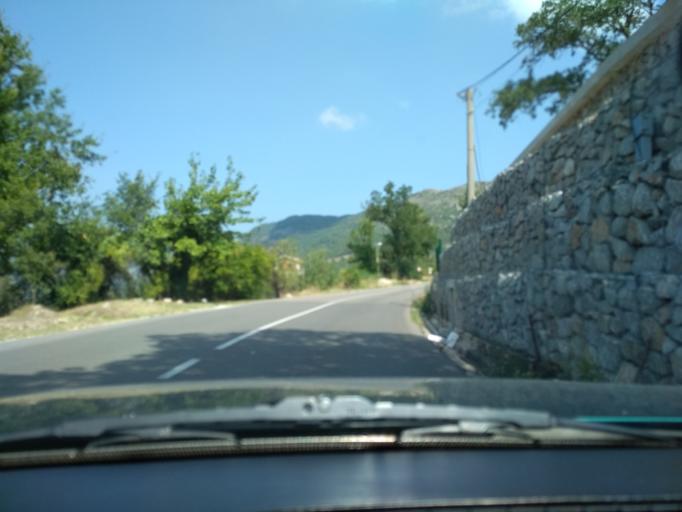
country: ME
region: Kotor
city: Kotor
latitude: 42.3946
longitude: 18.7549
